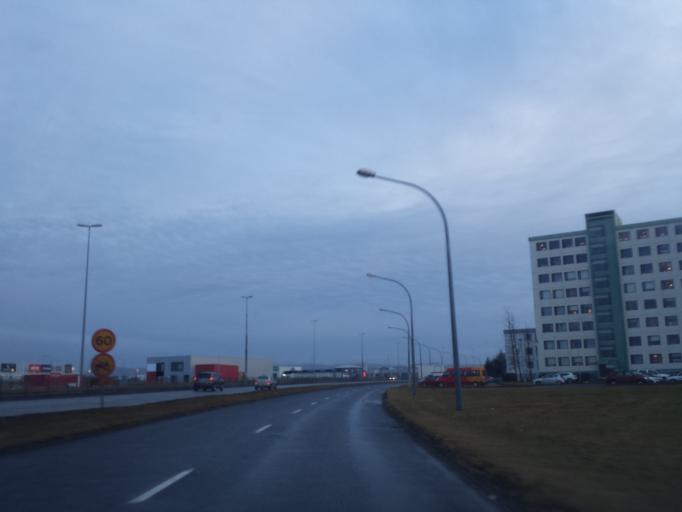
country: IS
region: Capital Region
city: Reykjavik
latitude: 64.1429
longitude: -21.8526
